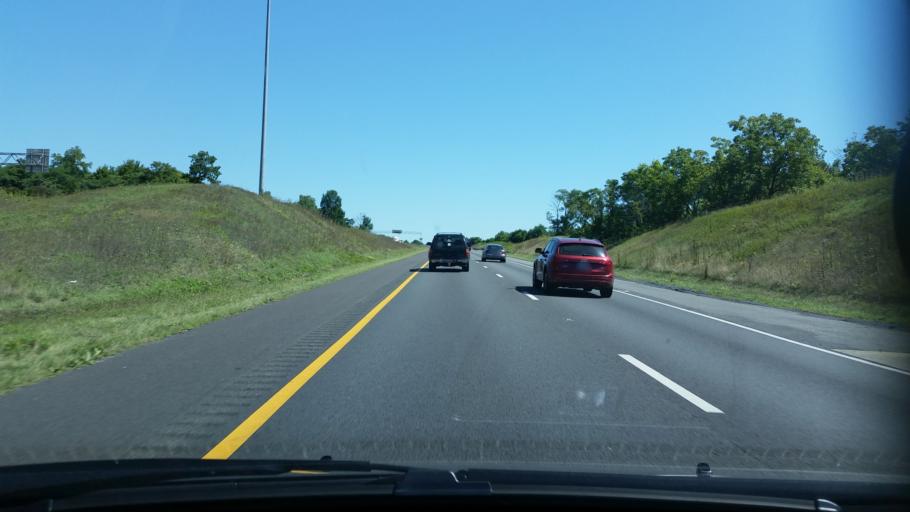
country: US
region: Virginia
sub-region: Frederick County
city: Stephens City
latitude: 39.0539
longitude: -78.2413
